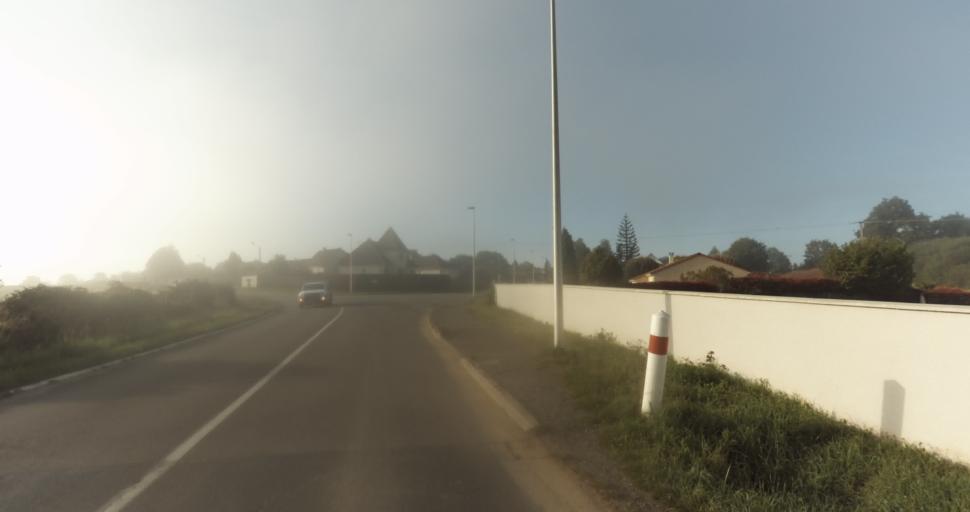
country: FR
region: Limousin
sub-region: Departement de la Haute-Vienne
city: Condat-sur-Vienne
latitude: 45.7874
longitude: 1.2867
